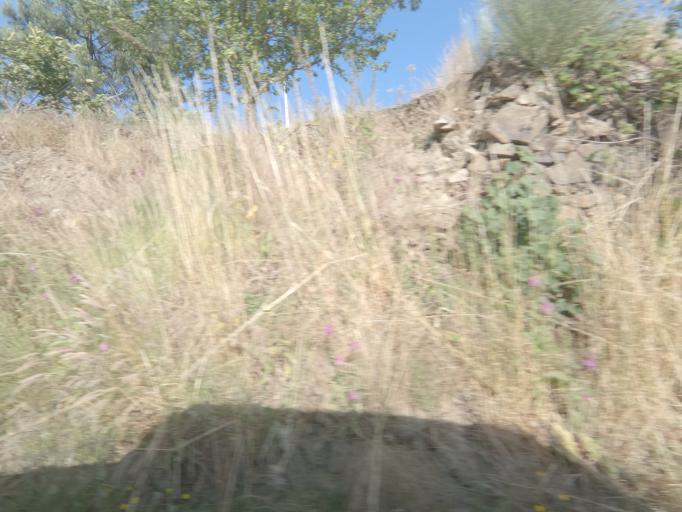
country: PT
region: Vila Real
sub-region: Sabrosa
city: Vilela
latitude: 41.1967
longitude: -7.6174
